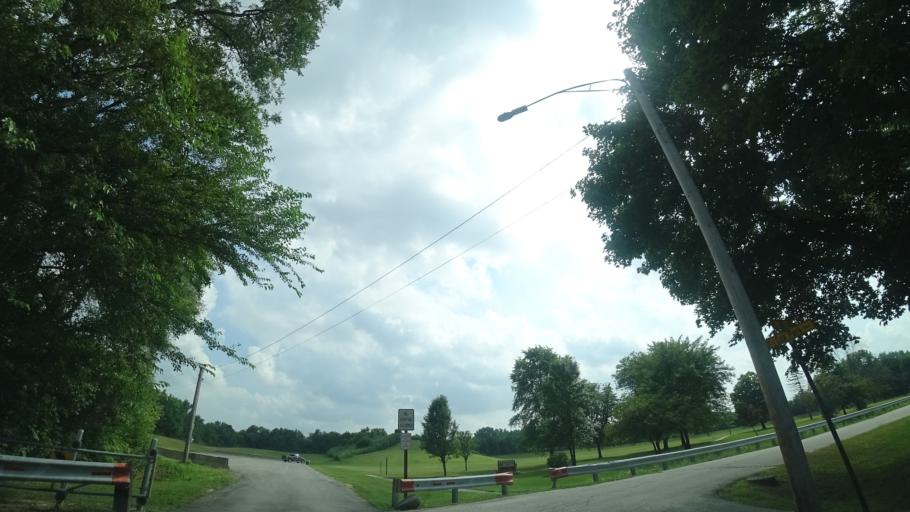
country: US
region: Illinois
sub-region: Cook County
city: Worth
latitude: 41.6811
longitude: -87.7881
